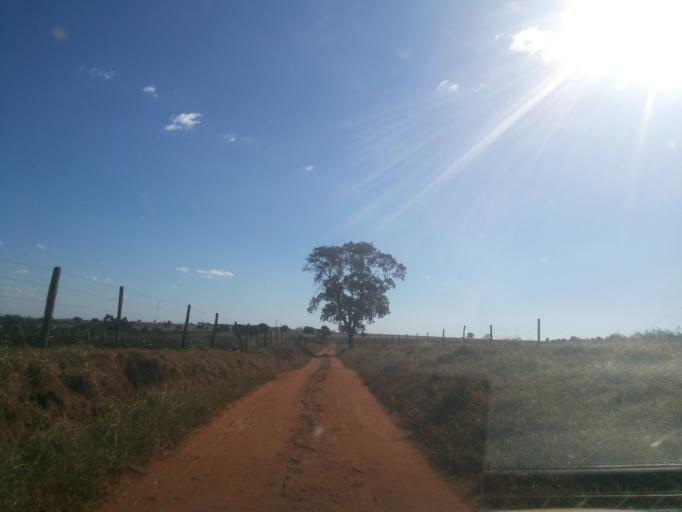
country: BR
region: Minas Gerais
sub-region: Centralina
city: Centralina
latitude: -18.7529
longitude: -49.1789
